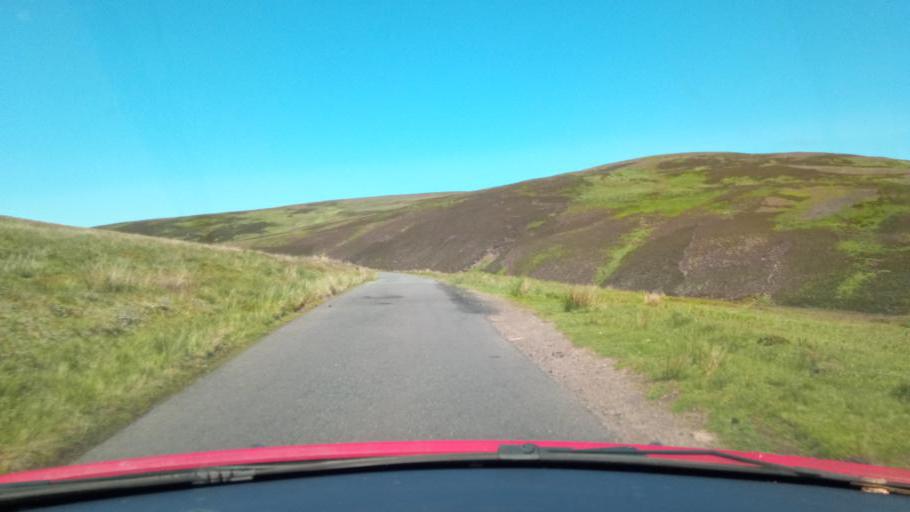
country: GB
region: Scotland
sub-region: East Lothian
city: East Linton
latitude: 55.8458
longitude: -2.5864
